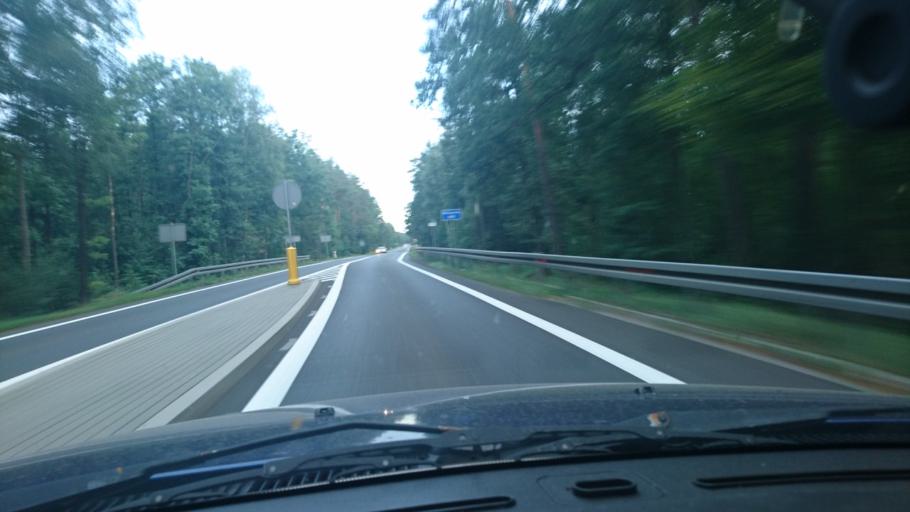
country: PL
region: Silesian Voivodeship
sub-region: Powiat lubliniecki
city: Lubliniec
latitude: 50.6104
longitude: 18.6942
